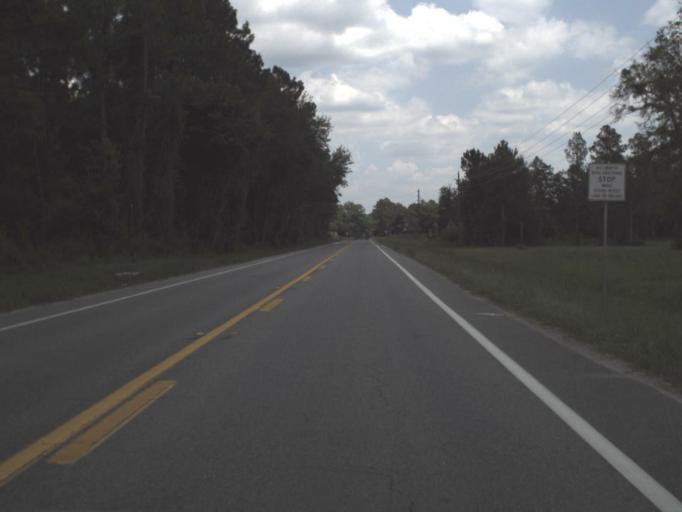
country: US
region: Florida
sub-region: Hamilton County
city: Jasper
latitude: 30.5212
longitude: -83.0559
